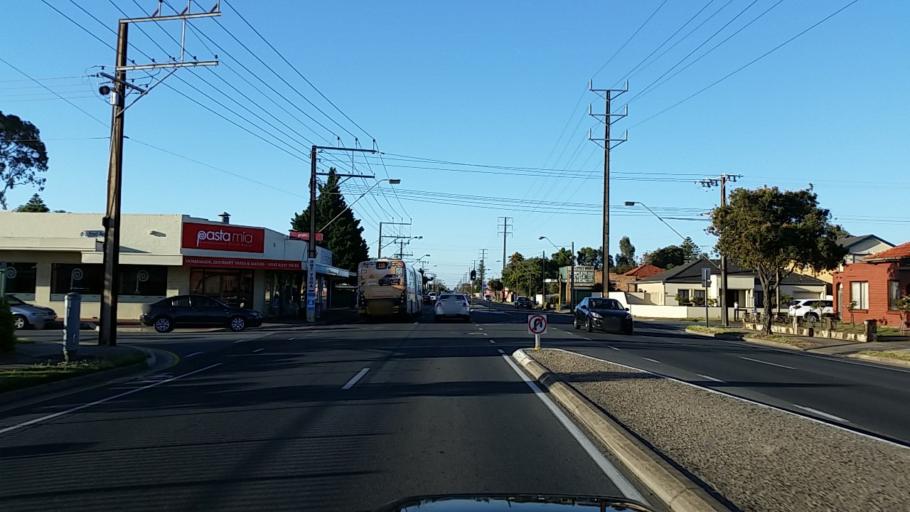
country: AU
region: South Australia
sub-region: Charles Sturt
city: Royal Park
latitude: -34.8859
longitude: 138.5132
